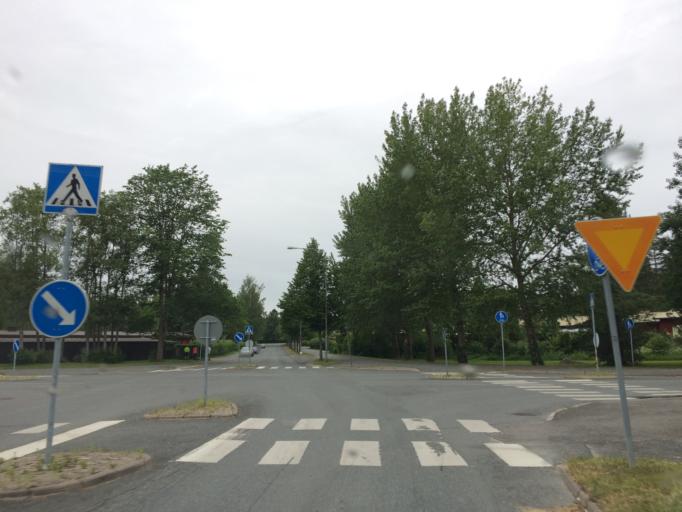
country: FI
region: Haeme
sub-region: Haemeenlinna
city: Haemeenlinna
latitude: 61.0115
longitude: 24.5022
